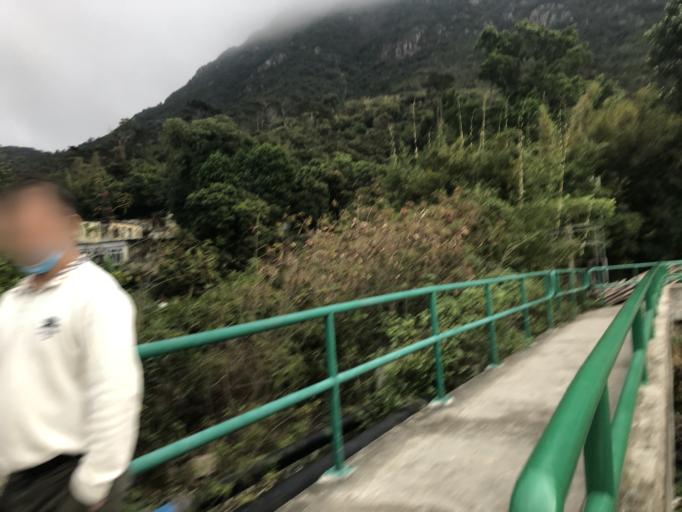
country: HK
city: Tai O
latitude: 22.2473
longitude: 113.8620
